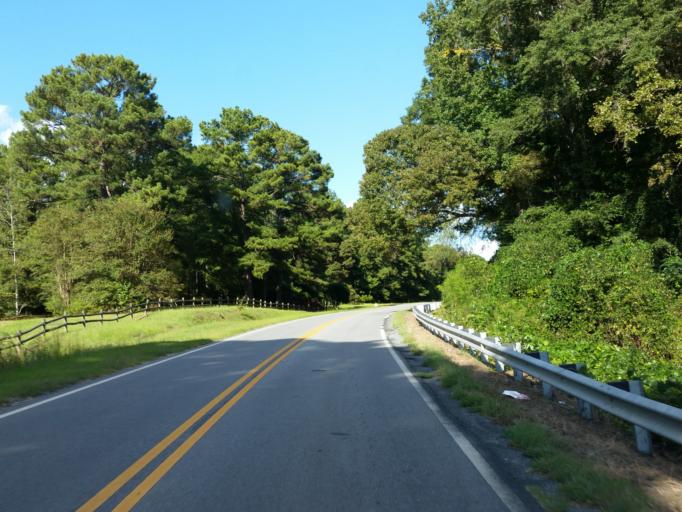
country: US
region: Georgia
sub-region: Butts County
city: Indian Springs
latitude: 33.1817
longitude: -84.0156
